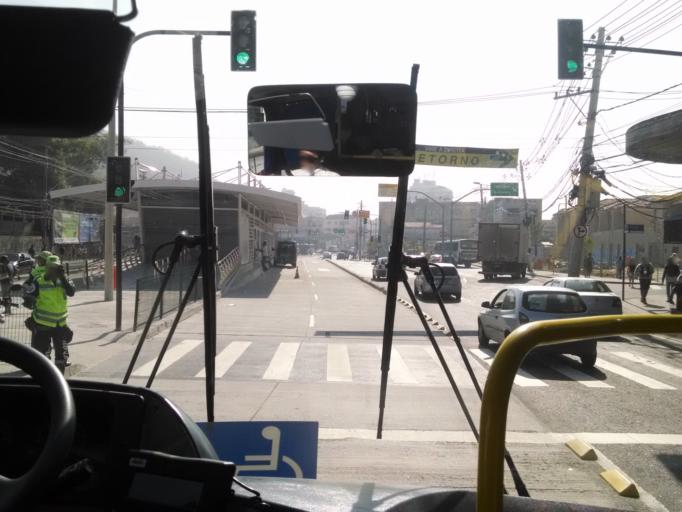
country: BR
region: Rio de Janeiro
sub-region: Sao Joao De Meriti
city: Sao Joao de Meriti
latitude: -22.8665
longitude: -43.3345
